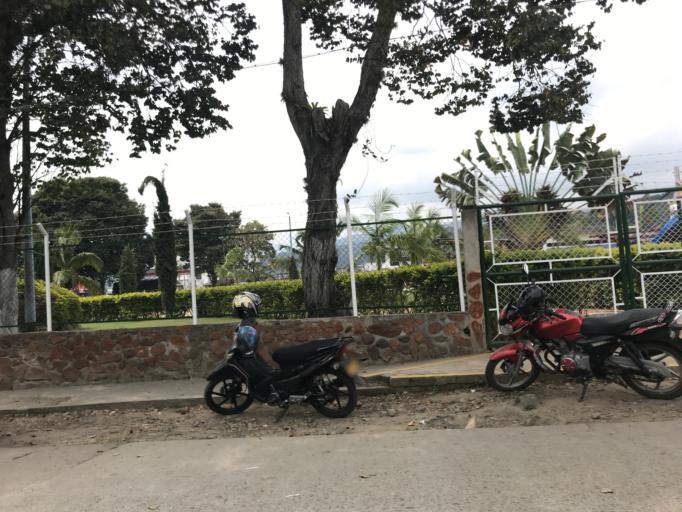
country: CO
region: Huila
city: San Agustin
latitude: 1.8798
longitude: -76.2701
